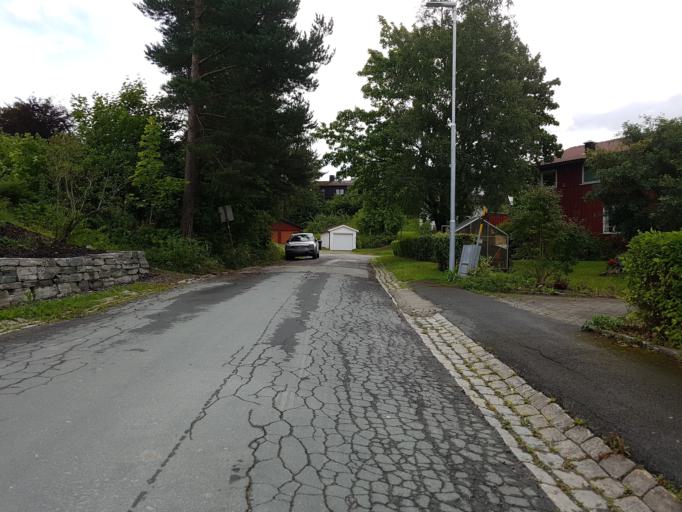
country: NO
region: Sor-Trondelag
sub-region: Trondheim
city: Trondheim
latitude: 63.4154
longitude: 10.4193
